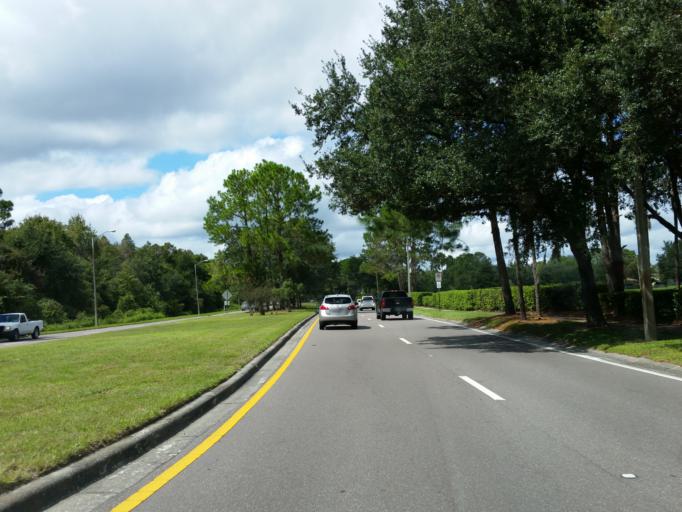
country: US
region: Florida
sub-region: Hillsborough County
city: Pebble Creek
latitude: 28.1428
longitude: -82.3473
